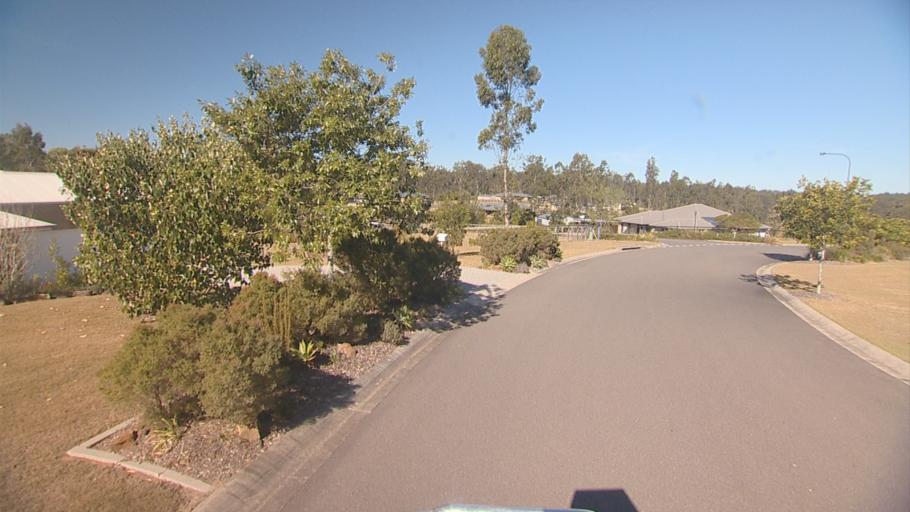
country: AU
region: Queensland
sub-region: Logan
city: North Maclean
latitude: -27.8266
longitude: 152.9837
